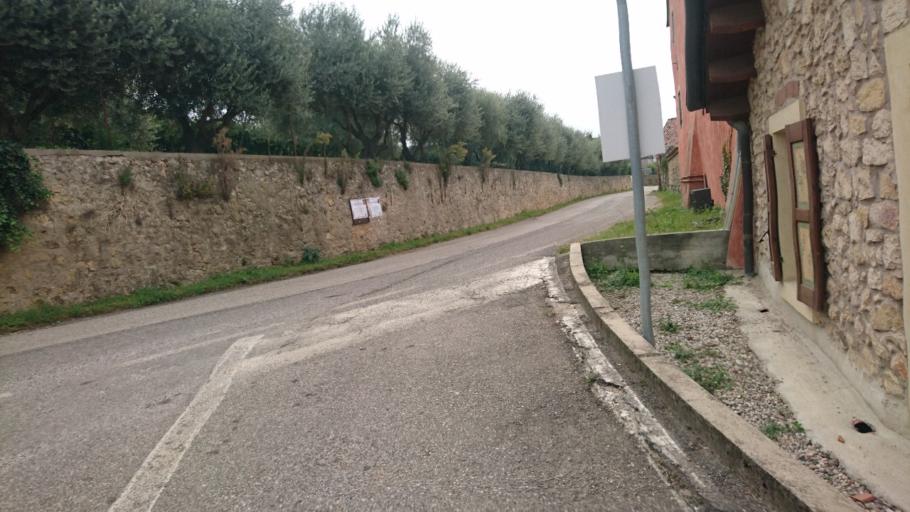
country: IT
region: Veneto
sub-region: Provincia di Verona
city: Soave
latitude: 45.4177
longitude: 11.2144
